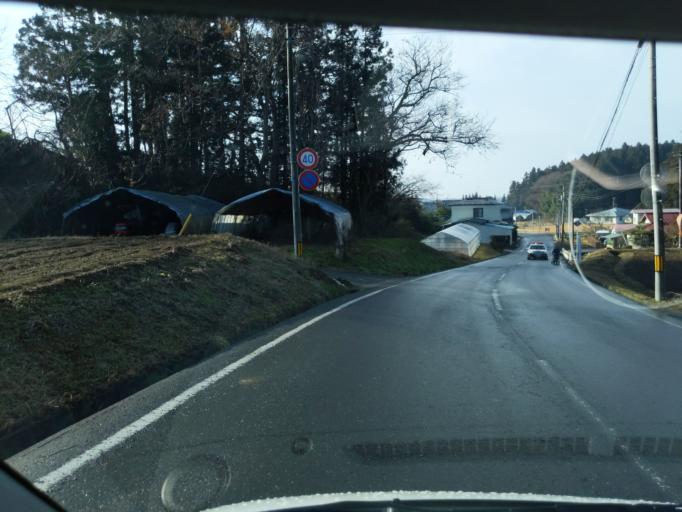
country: JP
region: Iwate
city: Ichinoseki
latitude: 38.7547
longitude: 141.1661
